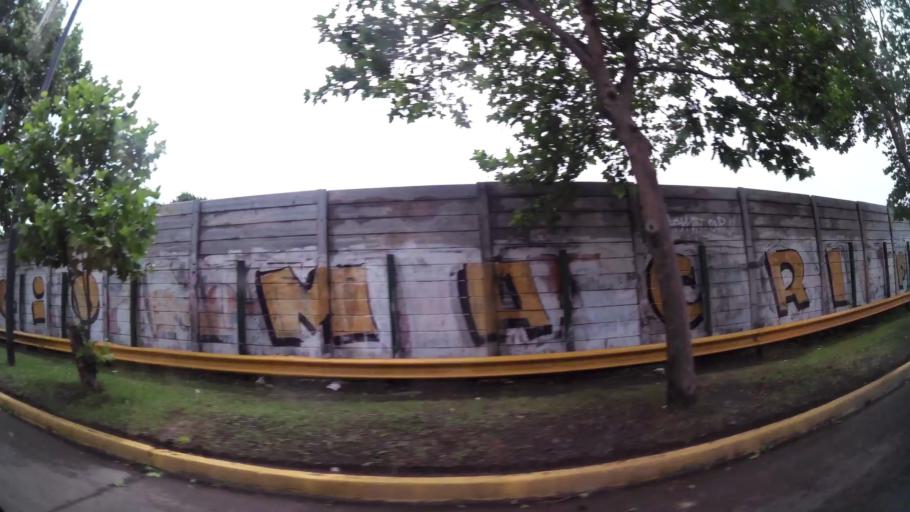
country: AR
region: Buenos Aires F.D.
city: Villa Lugano
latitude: -34.6678
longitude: -58.4526
